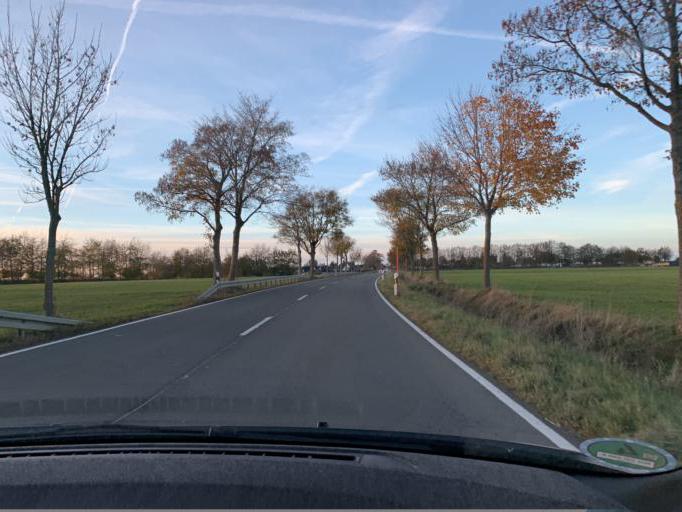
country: DE
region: North Rhine-Westphalia
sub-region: Regierungsbezirk Koln
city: Simmerath
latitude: 50.5987
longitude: 6.3435
